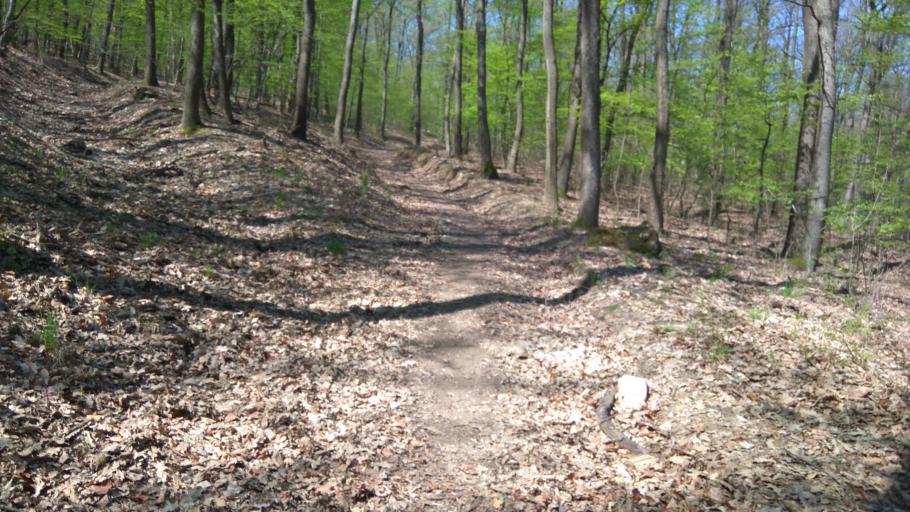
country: HU
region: Pest
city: Pilisborosjeno
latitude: 47.6257
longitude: 18.9918
